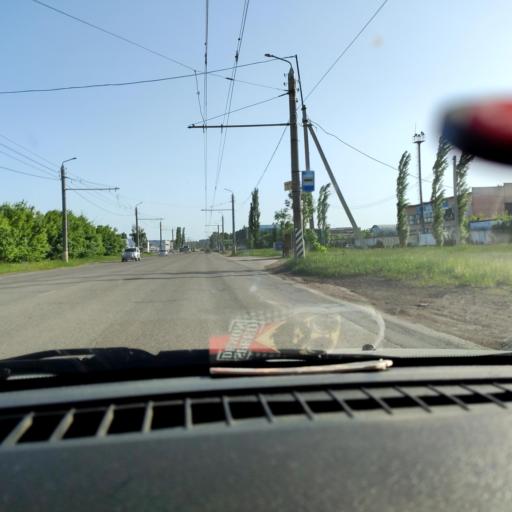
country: RU
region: Bashkortostan
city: Sterlitamak
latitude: 53.6489
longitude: 55.9148
